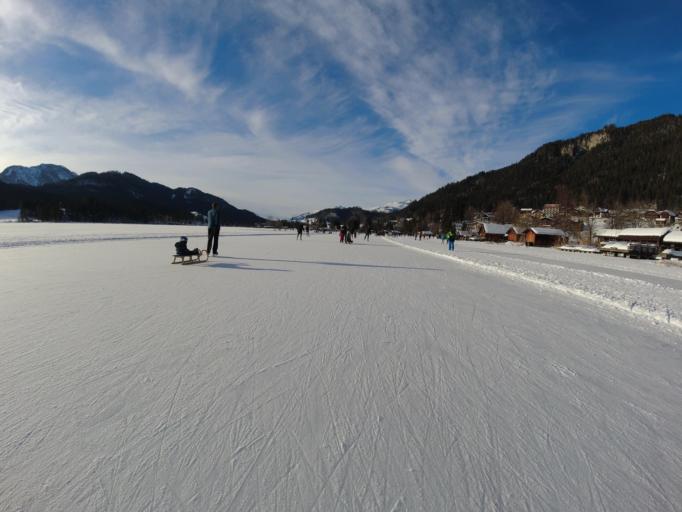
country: AT
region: Carinthia
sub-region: Politischer Bezirk Spittal an der Drau
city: Steinfeld
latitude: 46.7192
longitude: 13.2748
